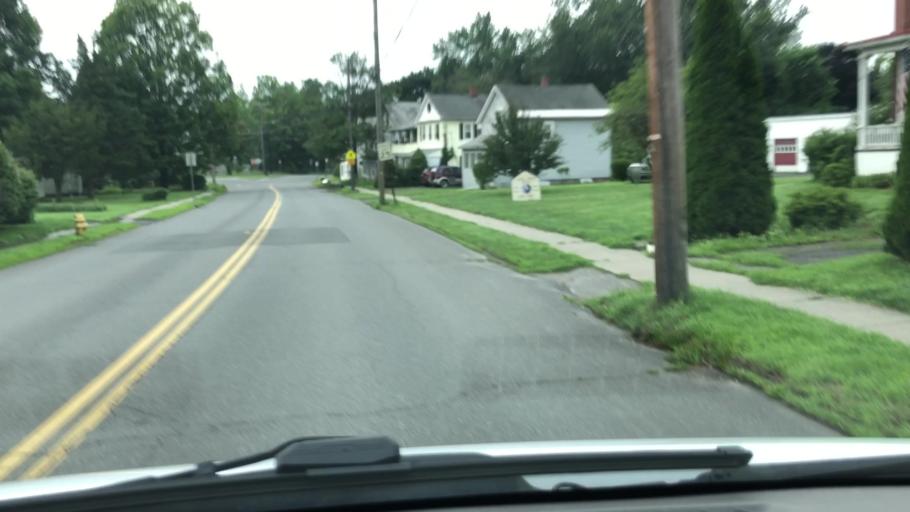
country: US
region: Massachusetts
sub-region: Franklin County
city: Greenfield
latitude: 42.5890
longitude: -72.6114
